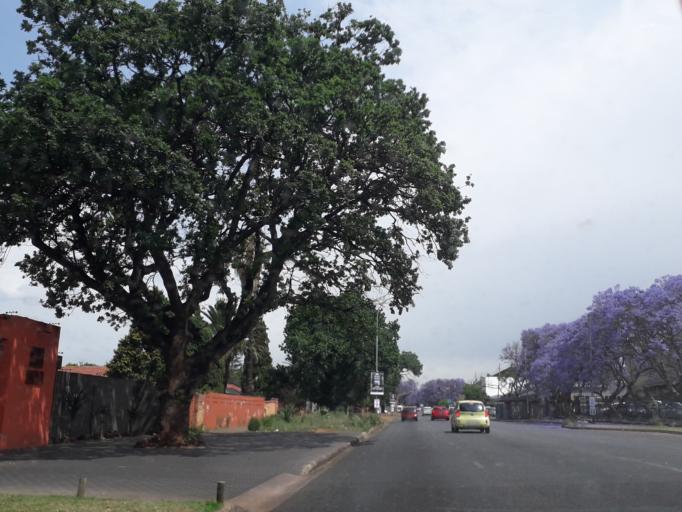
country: ZA
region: Gauteng
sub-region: City of Johannesburg Metropolitan Municipality
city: Johannesburg
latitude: -26.1597
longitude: 28.0123
